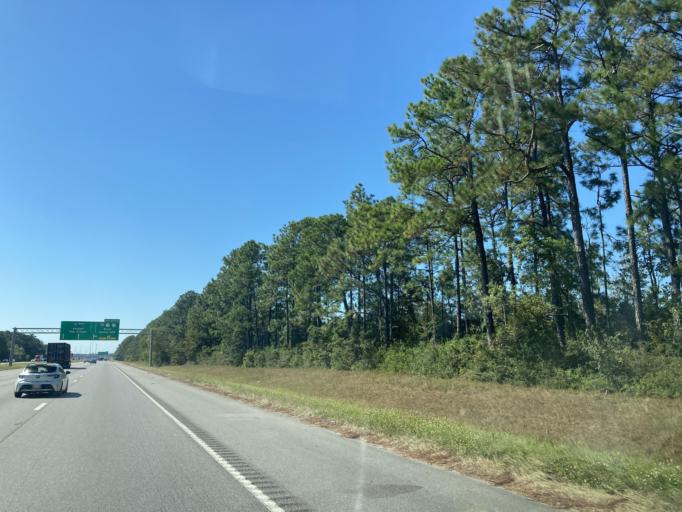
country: US
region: Mississippi
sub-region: Jackson County
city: Saint Martin
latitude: 30.4542
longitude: -88.8752
